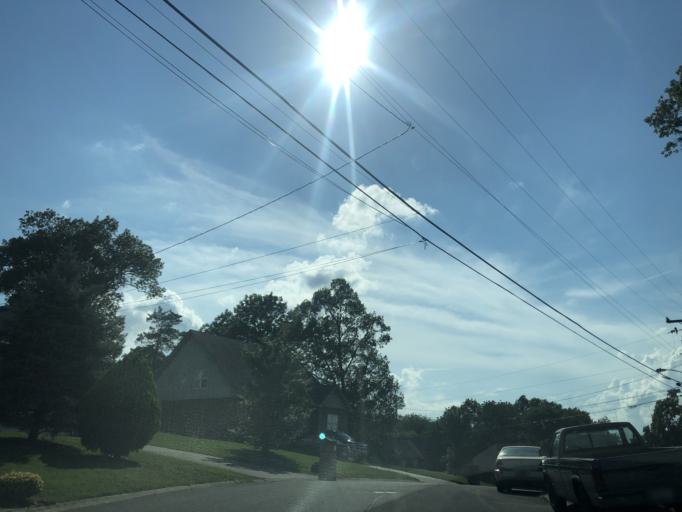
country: US
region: Tennessee
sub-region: Davidson County
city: Nashville
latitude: 36.2278
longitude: -86.8015
